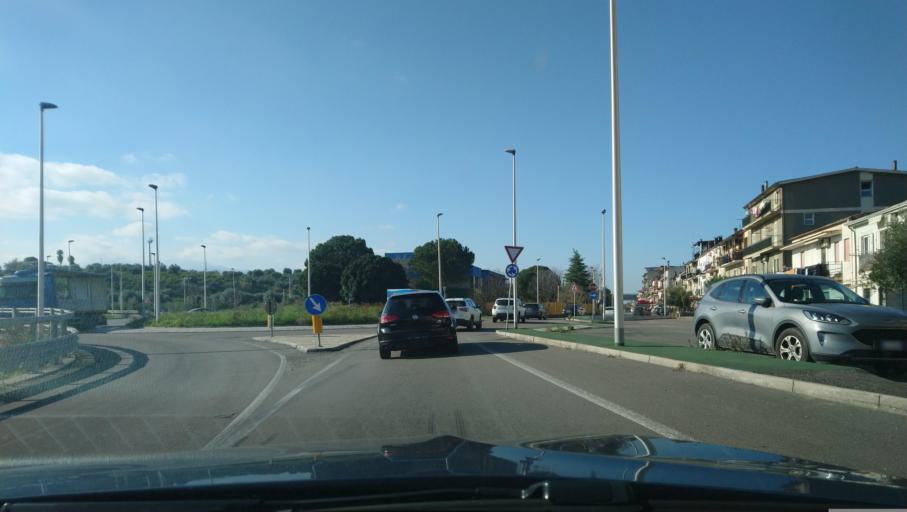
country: IT
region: Calabria
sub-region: Provincia di Cosenza
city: Amica
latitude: 39.6065
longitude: 16.7170
